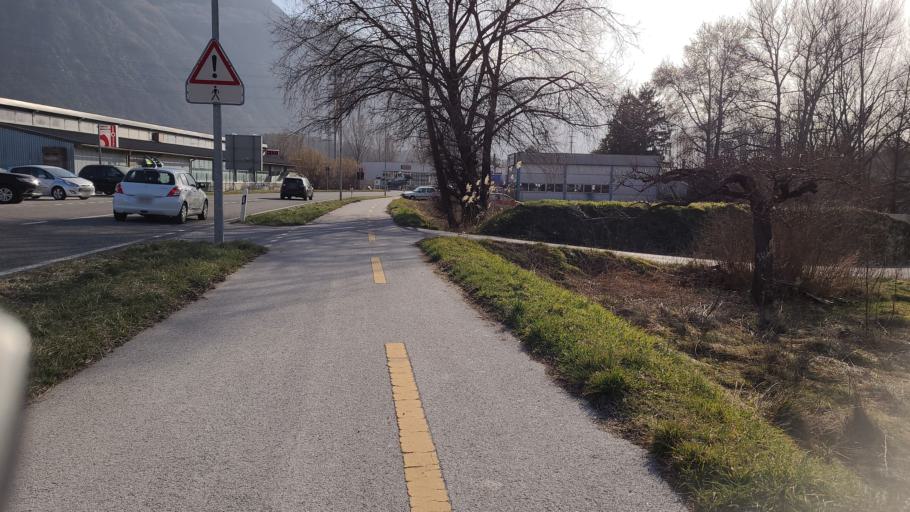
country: CH
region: Valais
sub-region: Leuk District
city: Salgesch
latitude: 46.3044
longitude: 7.5668
